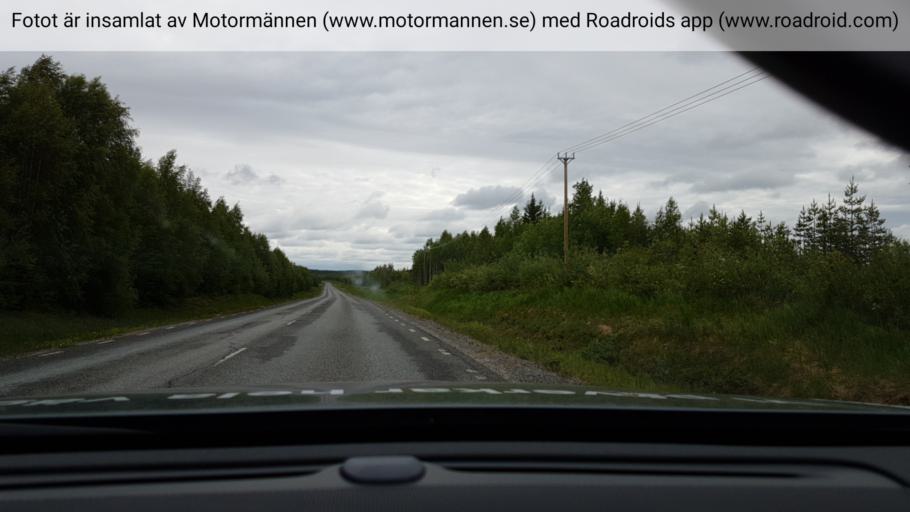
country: SE
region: Vaesterbotten
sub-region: Lycksele Kommun
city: Lycksele
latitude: 64.5326
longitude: 18.4715
